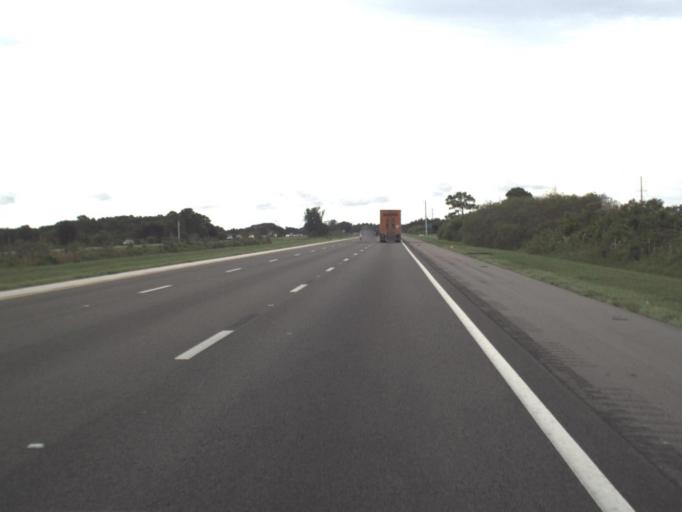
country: US
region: Florida
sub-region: Sarasota County
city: Laurel
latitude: 27.1812
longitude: -82.4367
